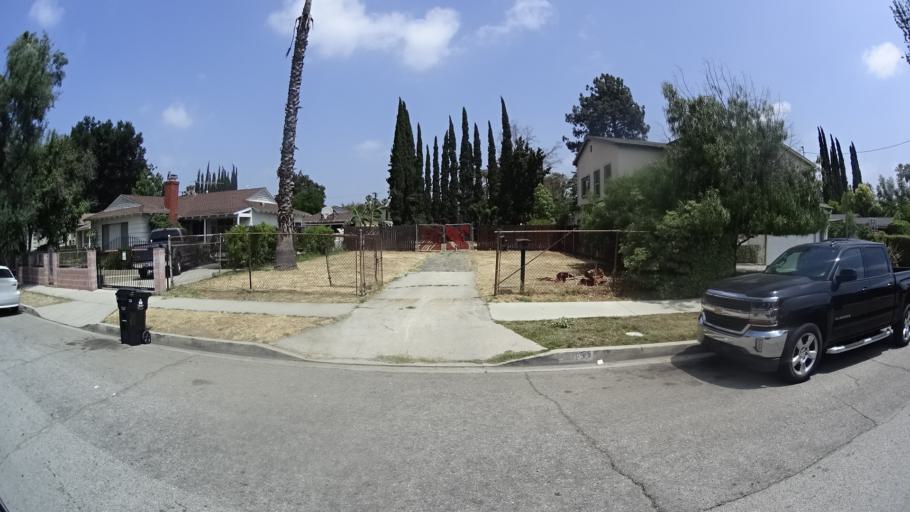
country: US
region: California
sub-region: Los Angeles County
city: Van Nuys
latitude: 34.1876
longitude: -118.4632
